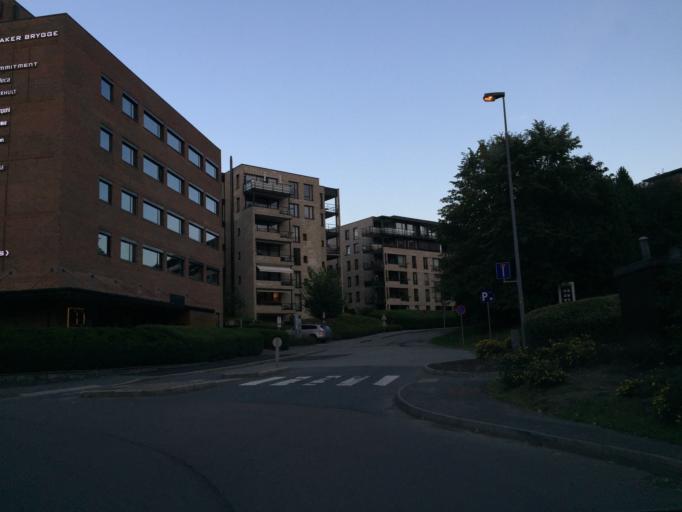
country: NO
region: Akershus
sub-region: Baerum
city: Lysaker
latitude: 59.9109
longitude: 10.6386
